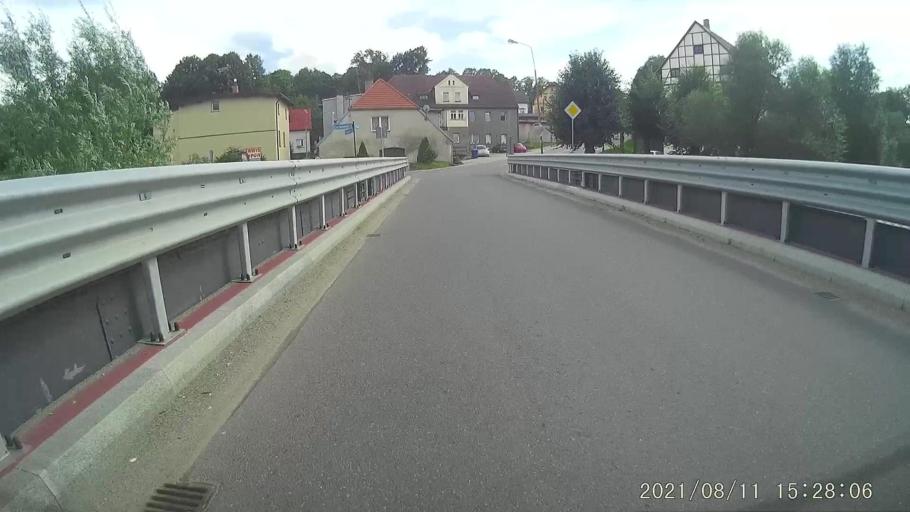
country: PL
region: Lower Silesian Voivodeship
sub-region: Powiat klodzki
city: Bystrzyca Klodzka
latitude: 50.2947
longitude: 16.6514
